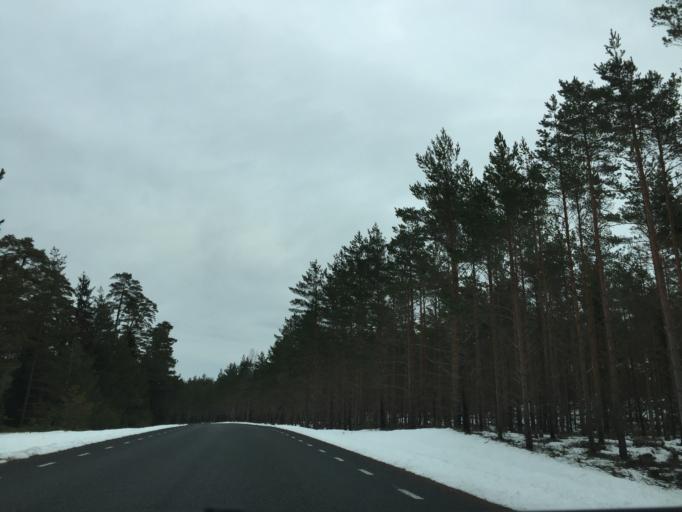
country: EE
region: Saare
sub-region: Kuressaare linn
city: Kuressaare
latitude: 58.4318
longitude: 22.2090
